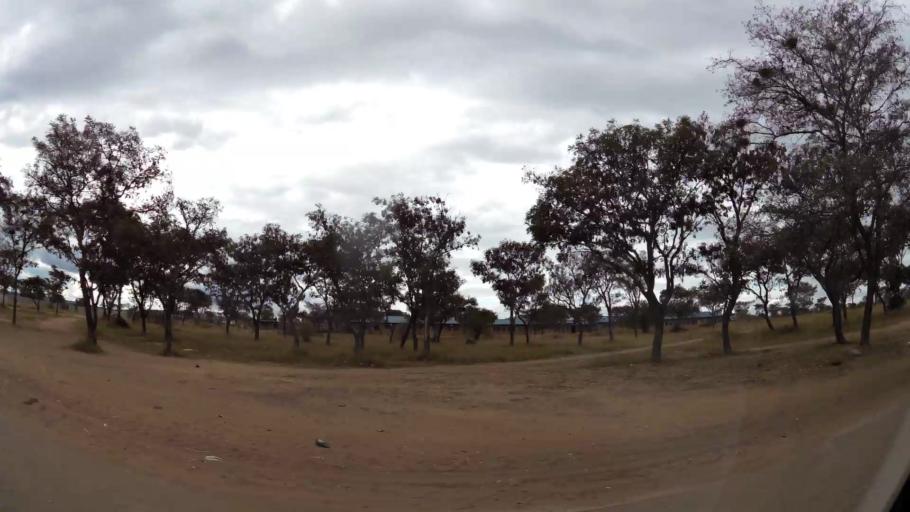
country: ZA
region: Limpopo
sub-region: Waterberg District Municipality
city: Modimolle
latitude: -24.6970
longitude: 28.4211
